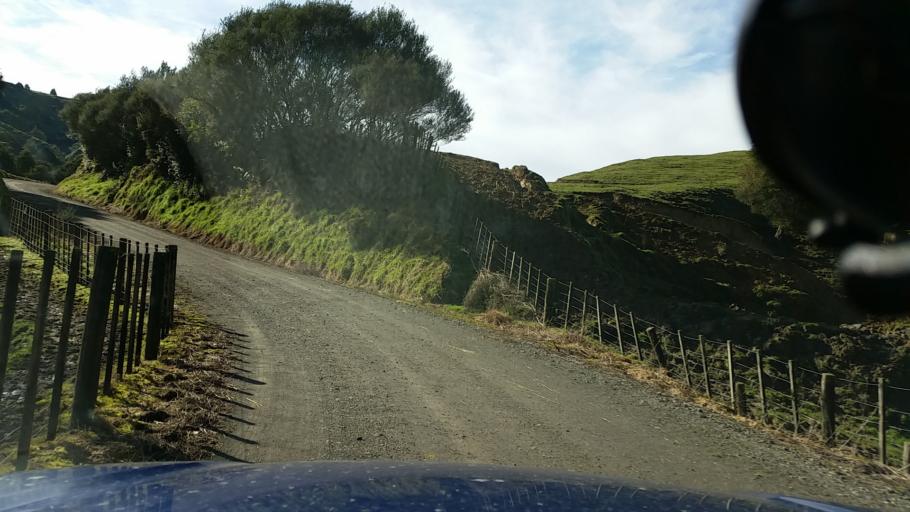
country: NZ
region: Taranaki
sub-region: New Plymouth District
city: Waitara
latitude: -39.0519
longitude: 174.7573
